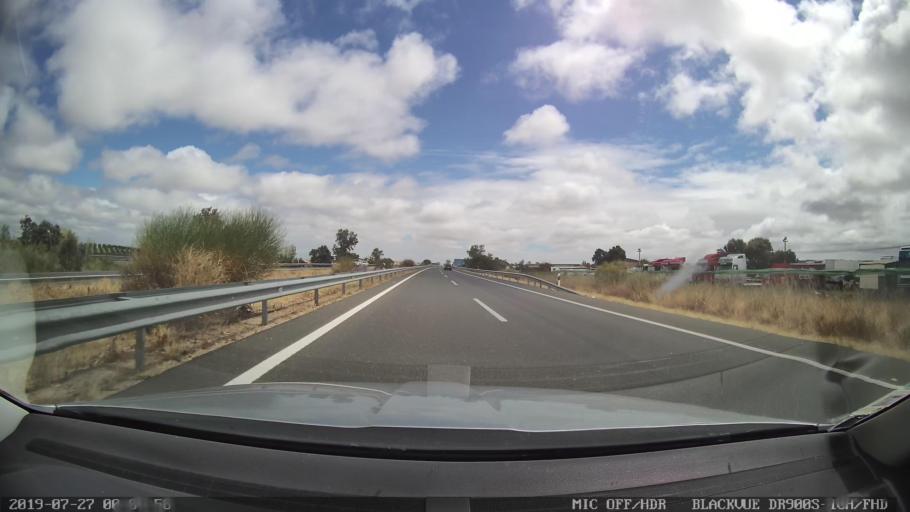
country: ES
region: Extremadura
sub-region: Provincia de Caceres
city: Saucedilla
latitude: 39.8440
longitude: -5.6398
